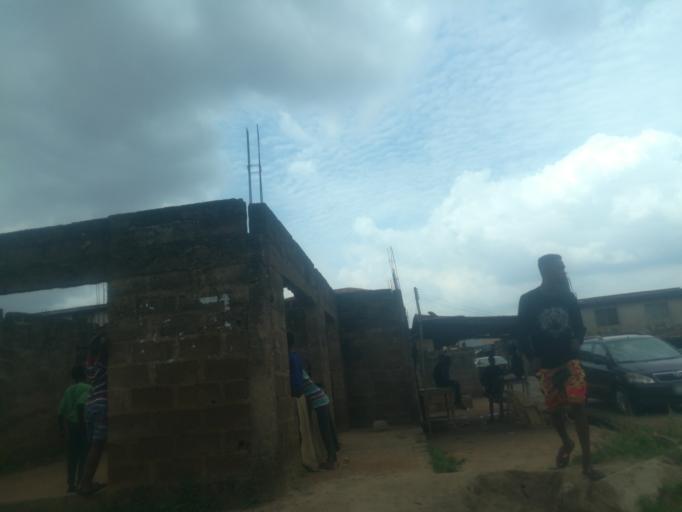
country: NG
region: Oyo
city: Ibadan
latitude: 7.4060
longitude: 3.9328
